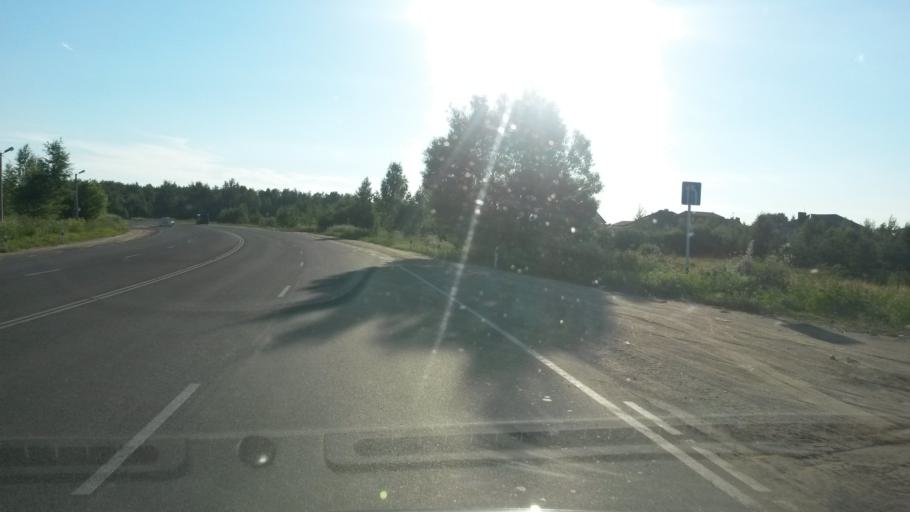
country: RU
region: Ivanovo
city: Novo-Talitsy
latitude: 57.0215
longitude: 40.8962
